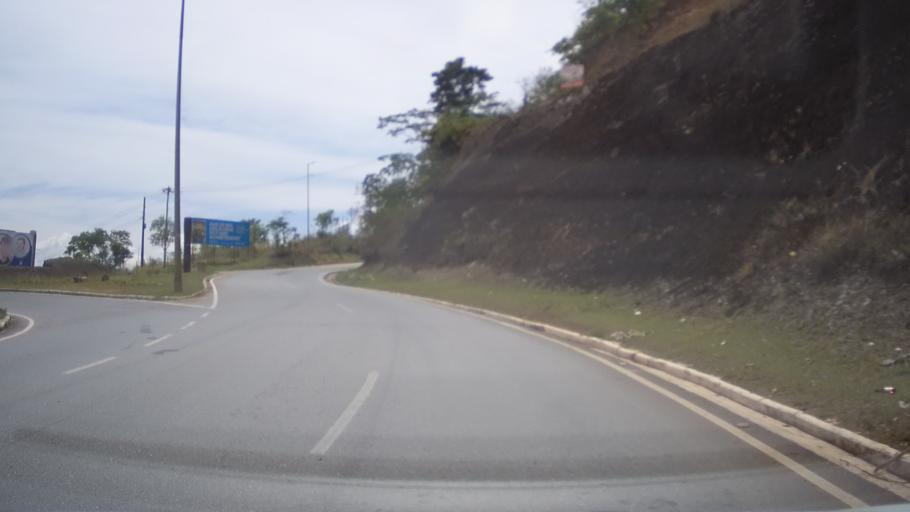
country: BR
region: Minas Gerais
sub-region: Nova Lima
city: Nova Lima
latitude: -19.9960
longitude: -43.8797
